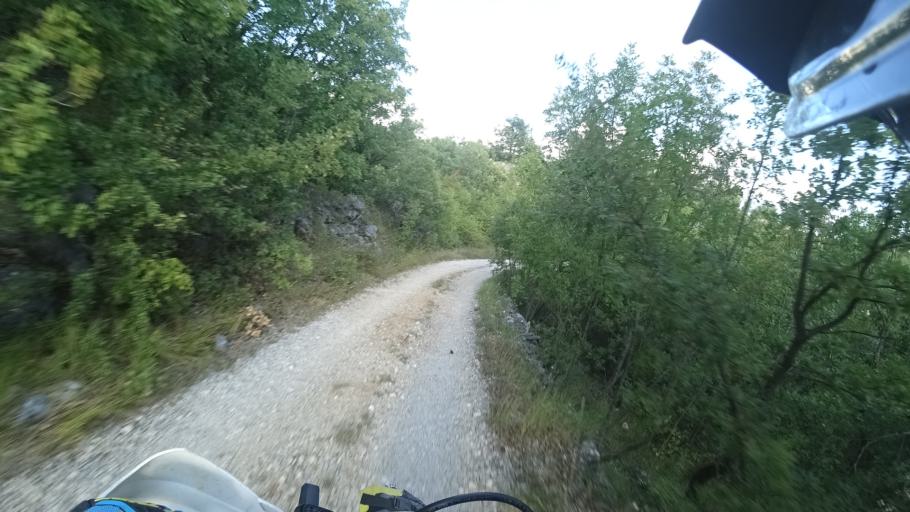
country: HR
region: Sibensko-Kniniska
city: Knin
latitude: 44.1376
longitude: 16.1150
